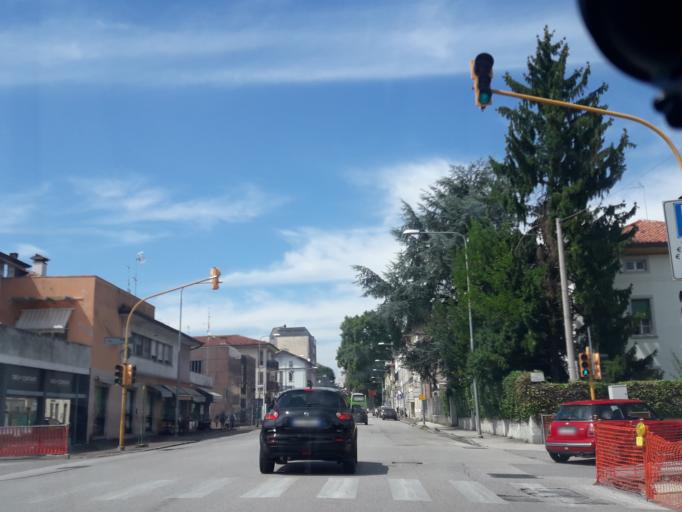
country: IT
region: Friuli Venezia Giulia
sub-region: Provincia di Udine
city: Udine
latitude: 46.0523
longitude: 13.2474
